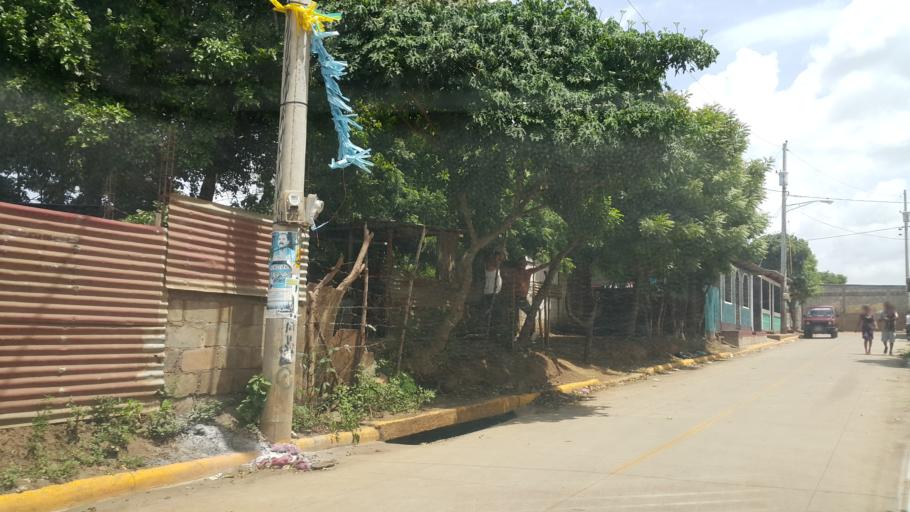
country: NI
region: Managua
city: Managua
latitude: 12.1159
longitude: -86.2417
